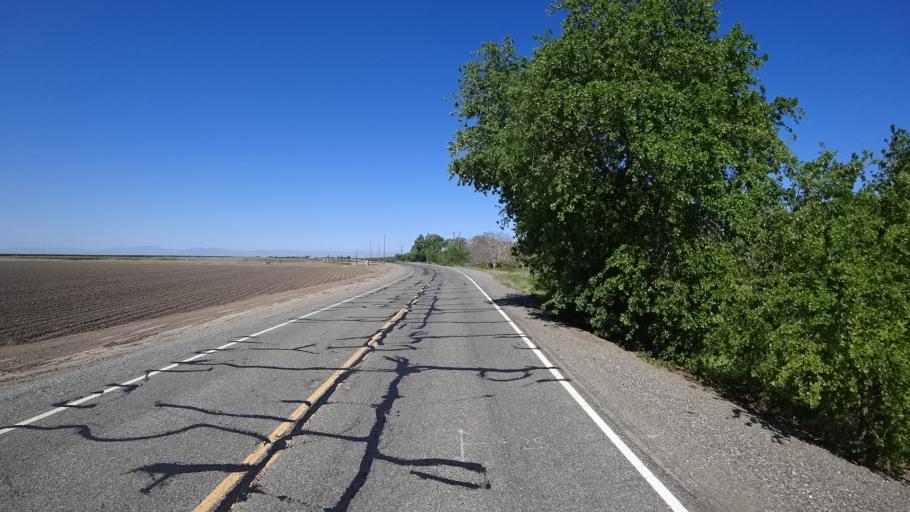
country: US
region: California
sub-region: Glenn County
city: Hamilton City
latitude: 39.7088
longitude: -122.0067
